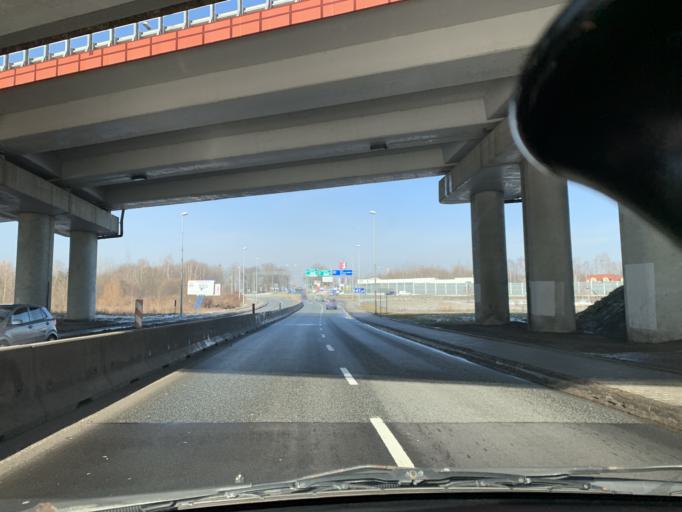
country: PL
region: Silesian Voivodeship
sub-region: Powiat tarnogorski
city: Radzionkow
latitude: 50.3739
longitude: 18.8922
